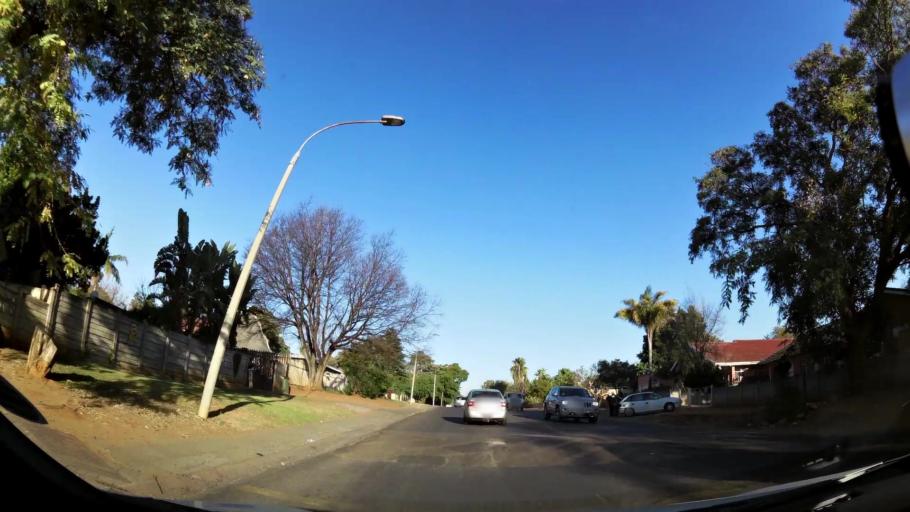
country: ZA
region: North-West
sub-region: Bojanala Platinum District Municipality
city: Rustenburg
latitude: -25.6784
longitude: 27.2145
